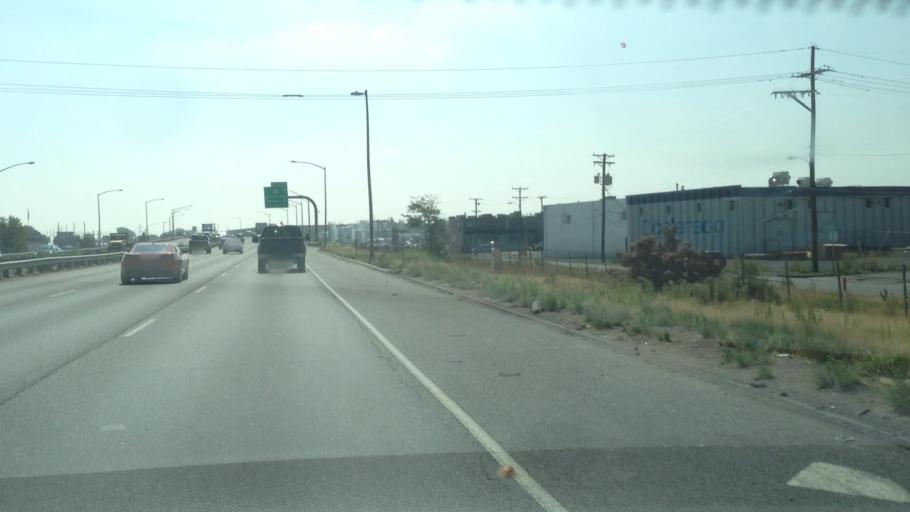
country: US
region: Colorado
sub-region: Adams County
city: Commerce City
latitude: 39.7790
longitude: -104.9264
